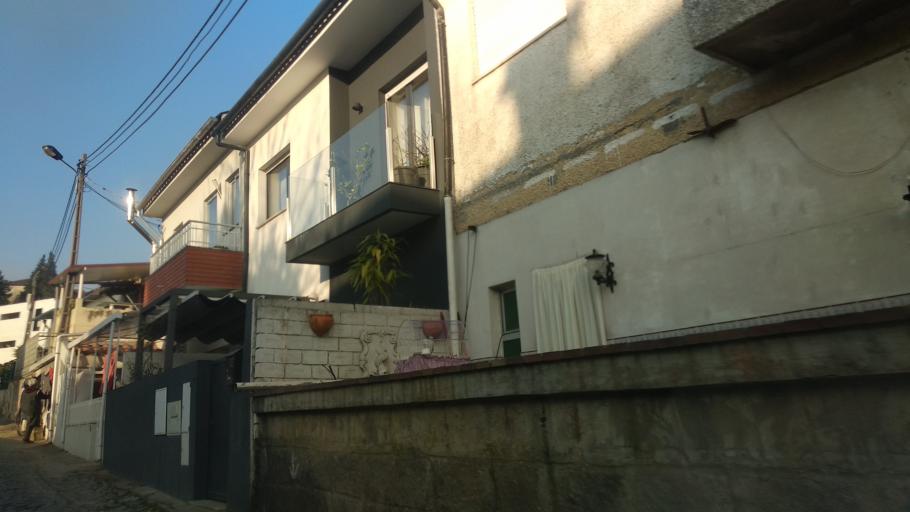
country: PT
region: Braga
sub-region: Braga
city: Adaufe
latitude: 41.5701
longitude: -8.3789
